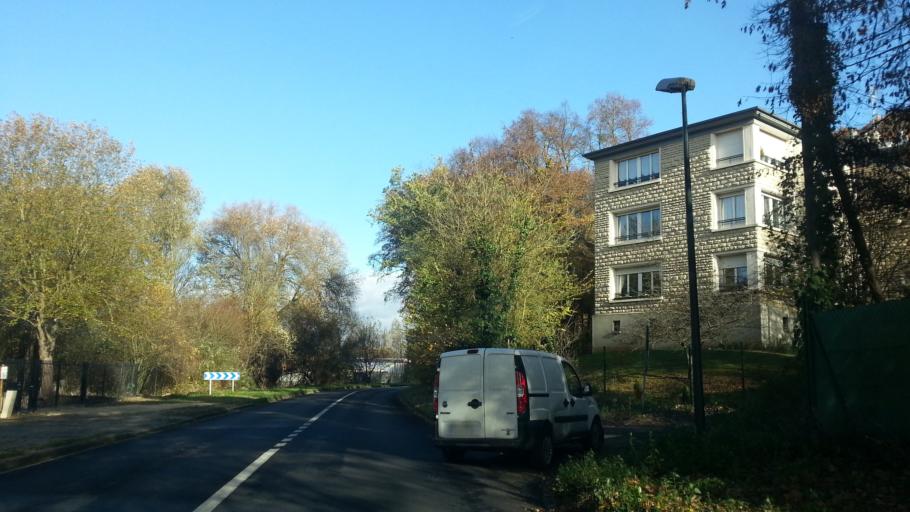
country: FR
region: Picardie
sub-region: Departement de l'Oise
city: Villers-Saint-Paul
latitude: 49.2753
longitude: 2.4993
